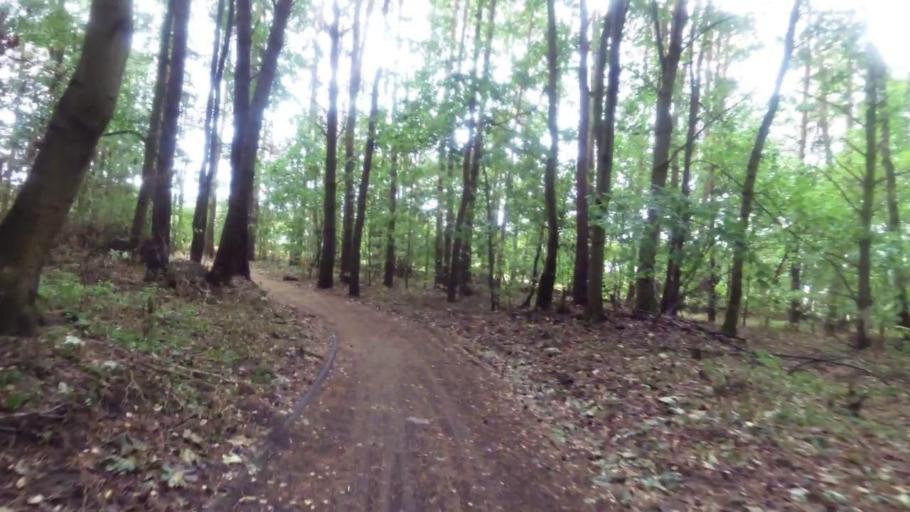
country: PL
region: West Pomeranian Voivodeship
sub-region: Powiat mysliborski
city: Debno
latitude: 52.7204
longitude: 14.6929
